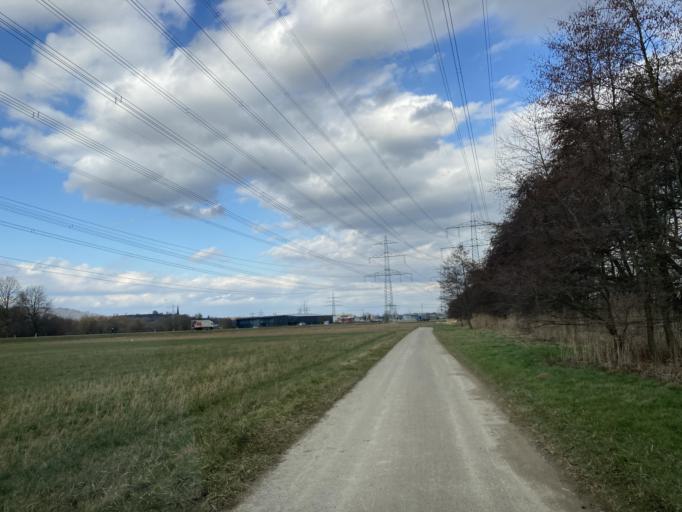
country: DE
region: Baden-Wuerttemberg
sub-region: Freiburg Region
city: Eichstetten
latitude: 48.0845
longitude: 7.7548
